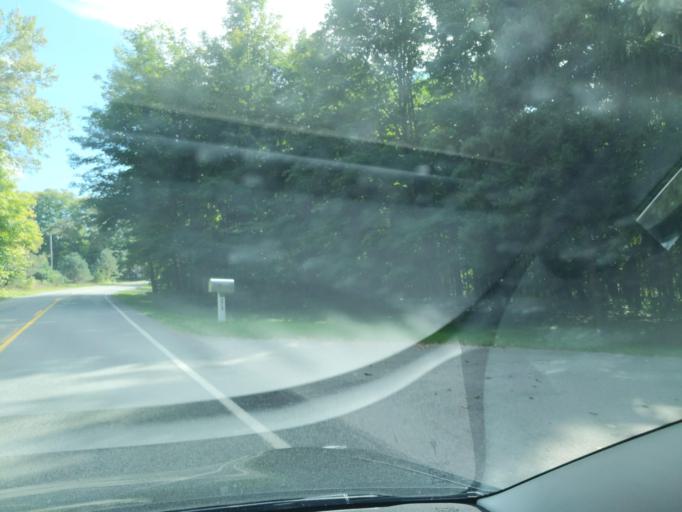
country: US
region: Michigan
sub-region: Antrim County
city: Bellaire
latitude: 44.9903
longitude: -85.2851
